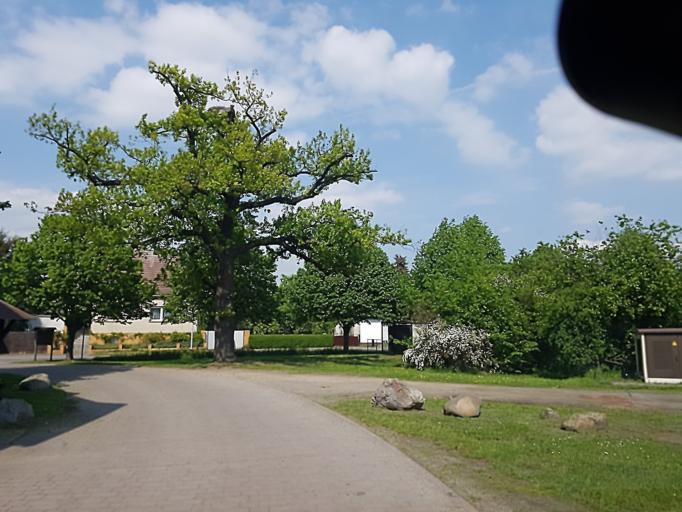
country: DE
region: Brandenburg
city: Doberlug-Kirchhain
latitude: 51.6121
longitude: 13.5891
